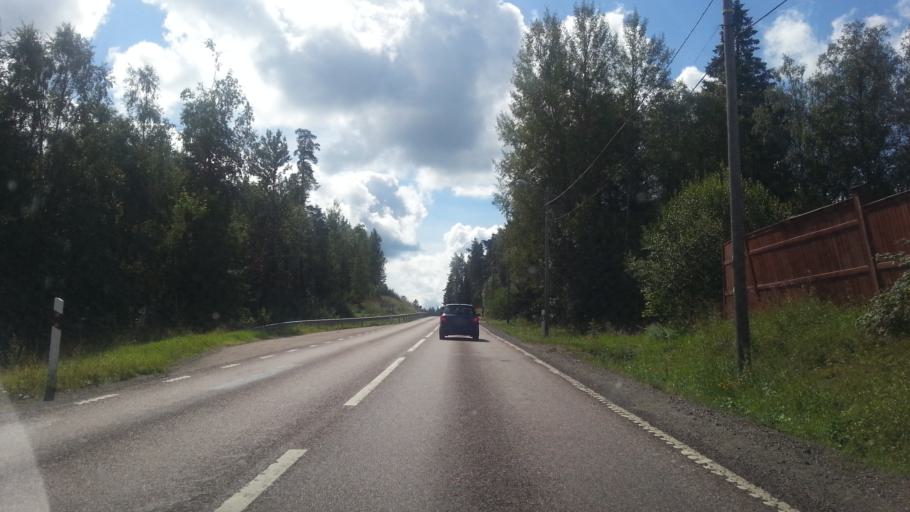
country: SE
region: Dalarna
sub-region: Ludvika Kommun
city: Grangesberg
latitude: 60.0630
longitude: 14.9860
